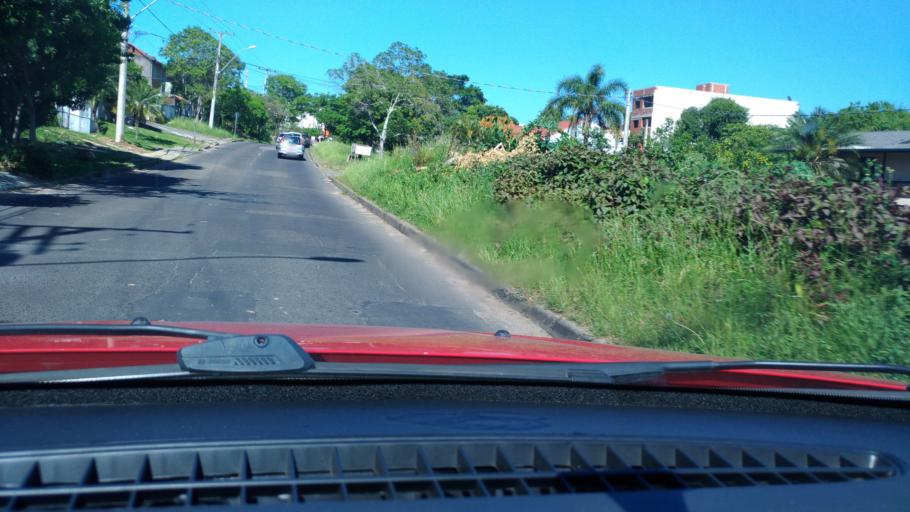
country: BR
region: Rio Grande do Sul
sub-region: Porto Alegre
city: Porto Alegre
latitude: -30.0332
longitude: -51.1485
